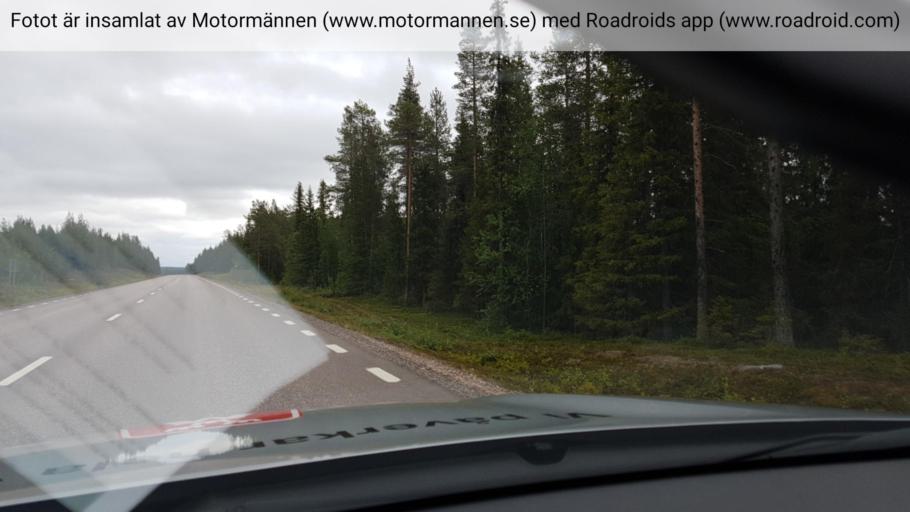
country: SE
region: Norrbotten
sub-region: Gallivare Kommun
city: Gaellivare
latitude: 67.0803
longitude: 21.0598
